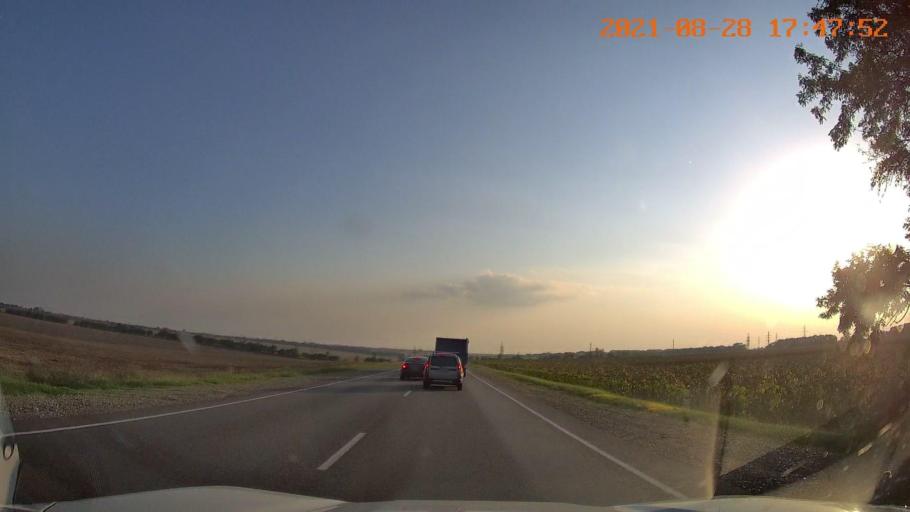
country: RU
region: Krasnodarskiy
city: Novoalekseyevskaya
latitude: 44.9685
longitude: 40.8466
